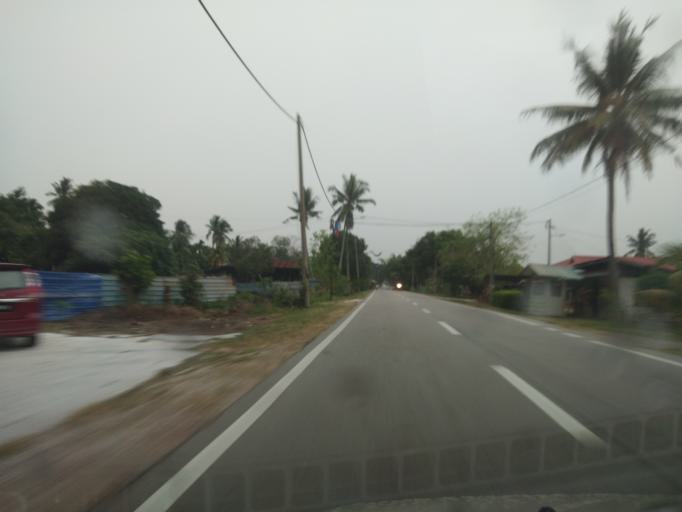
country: MY
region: Penang
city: Kepala Batas
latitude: 5.4985
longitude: 100.3963
